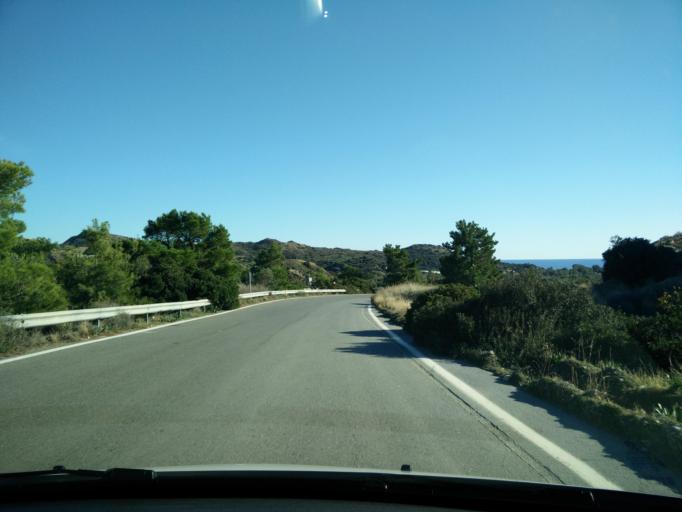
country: GR
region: Crete
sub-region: Nomos Lasithiou
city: Gra Liyia
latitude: 35.0161
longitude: 25.5826
